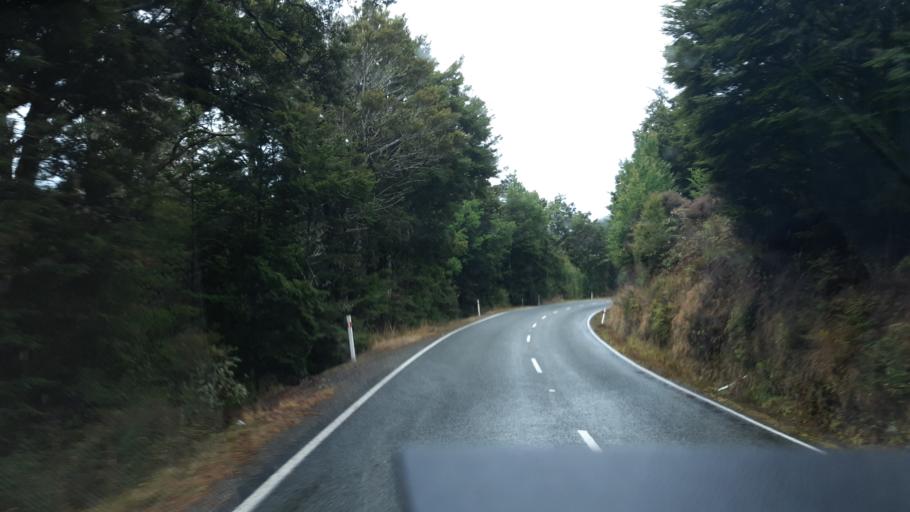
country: NZ
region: Tasman
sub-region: Tasman District
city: Wakefield
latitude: -41.7558
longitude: 172.8967
